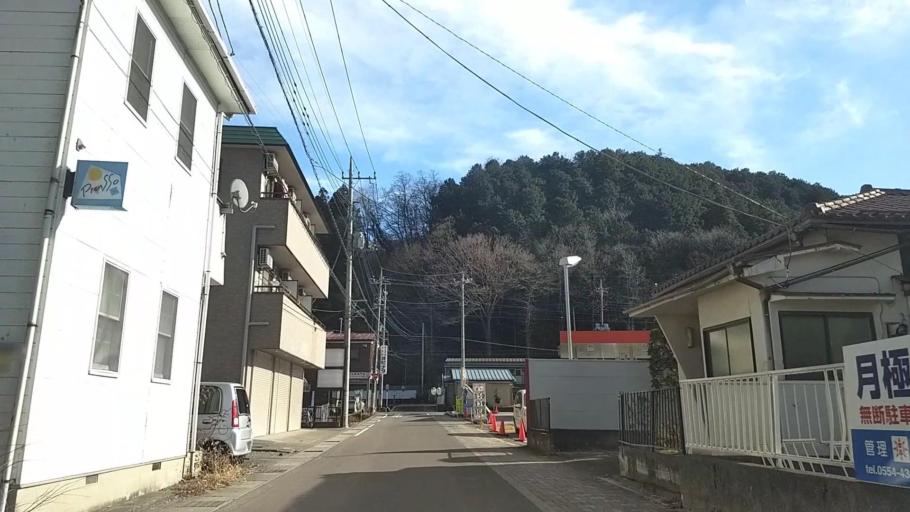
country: JP
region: Yamanashi
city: Otsuki
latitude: 35.5460
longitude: 138.9047
